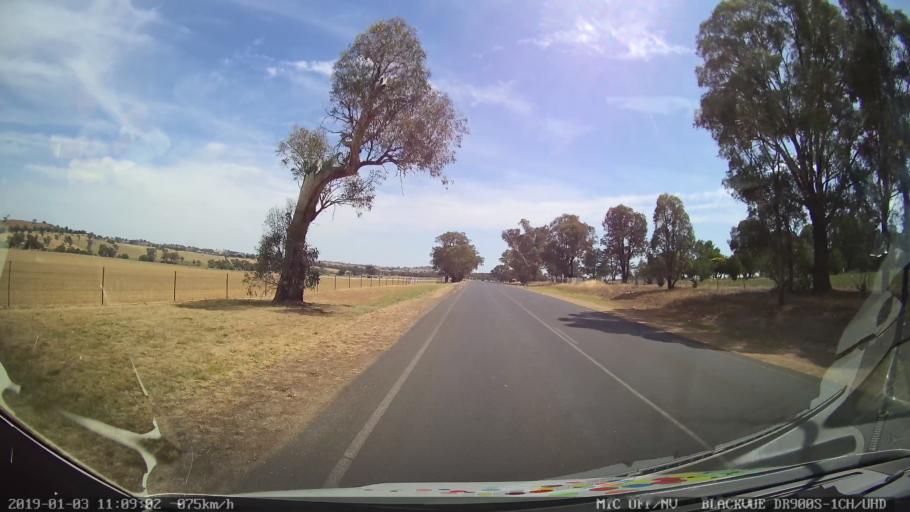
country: AU
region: New South Wales
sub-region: Young
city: Young
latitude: -34.2430
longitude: 148.2555
